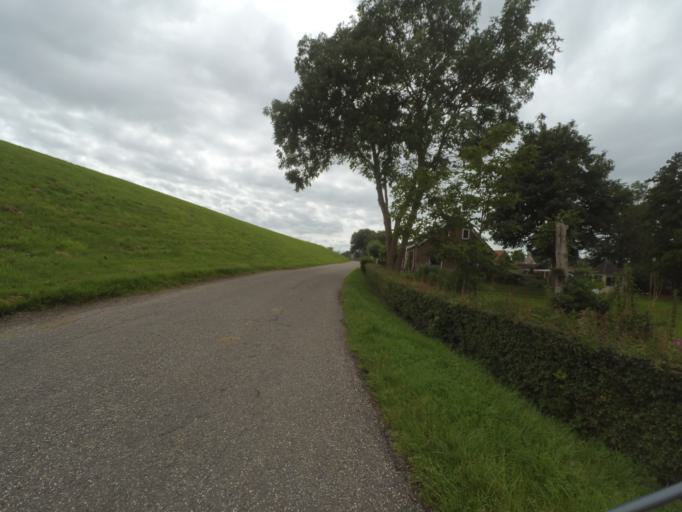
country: NL
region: Friesland
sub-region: Gemeente Dongeradeel
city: Anjum
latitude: 53.3600
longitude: 6.1500
